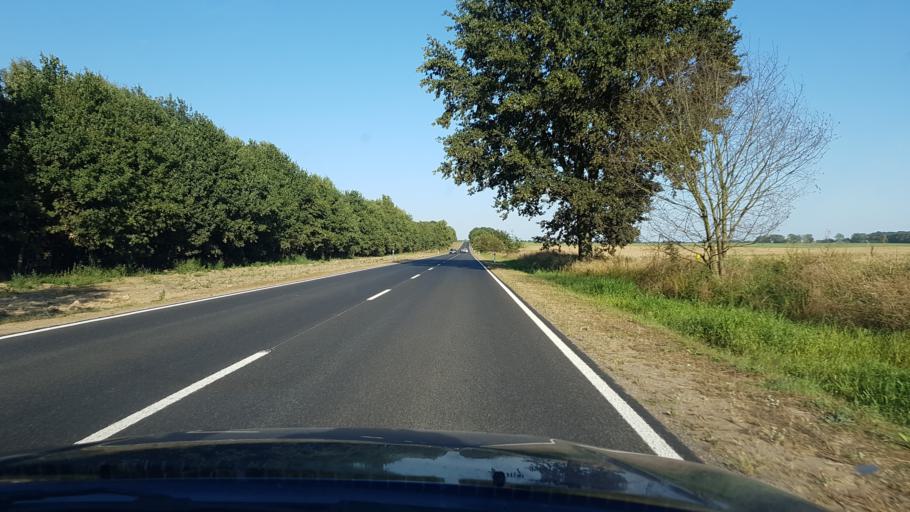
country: PL
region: West Pomeranian Voivodeship
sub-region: Powiat goleniowski
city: Maszewo
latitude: 53.4312
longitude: 15.0303
